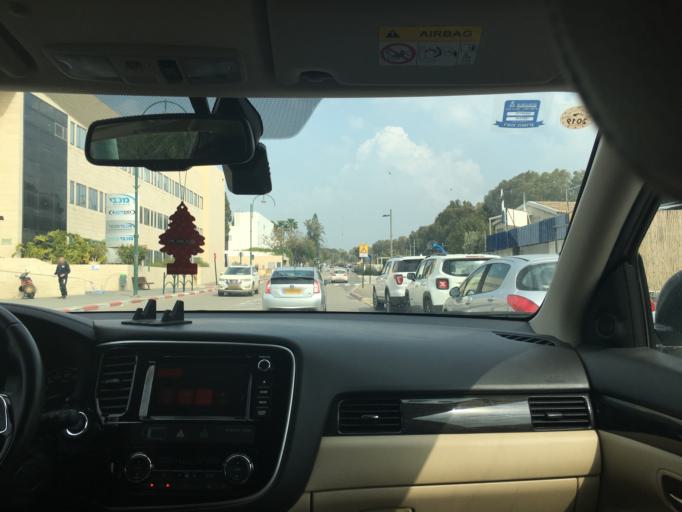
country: IL
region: Tel Aviv
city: Ramat HaSharon
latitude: 32.1380
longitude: 34.8437
